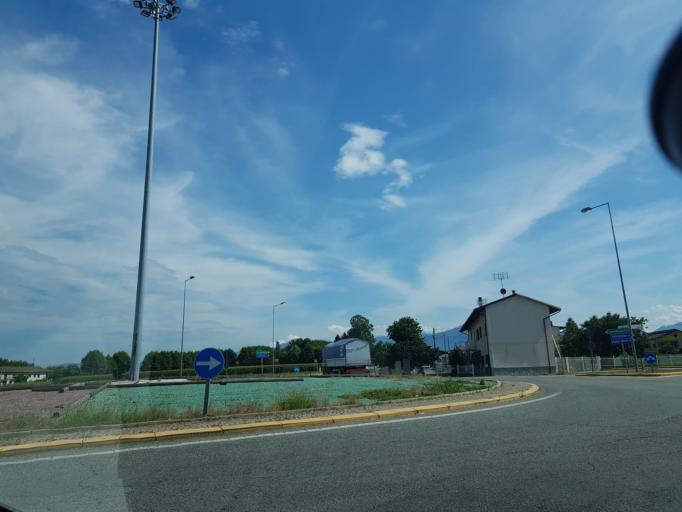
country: IT
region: Piedmont
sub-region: Provincia di Cuneo
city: Roata Rossi
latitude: 44.4477
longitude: 7.5272
